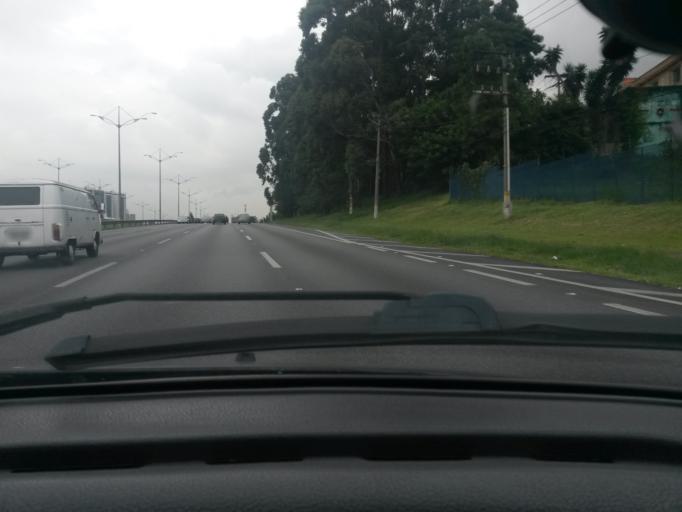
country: BR
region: Sao Paulo
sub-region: Sao Bernardo Do Campo
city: Sao Bernardo do Campo
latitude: -23.6789
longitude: -46.5689
